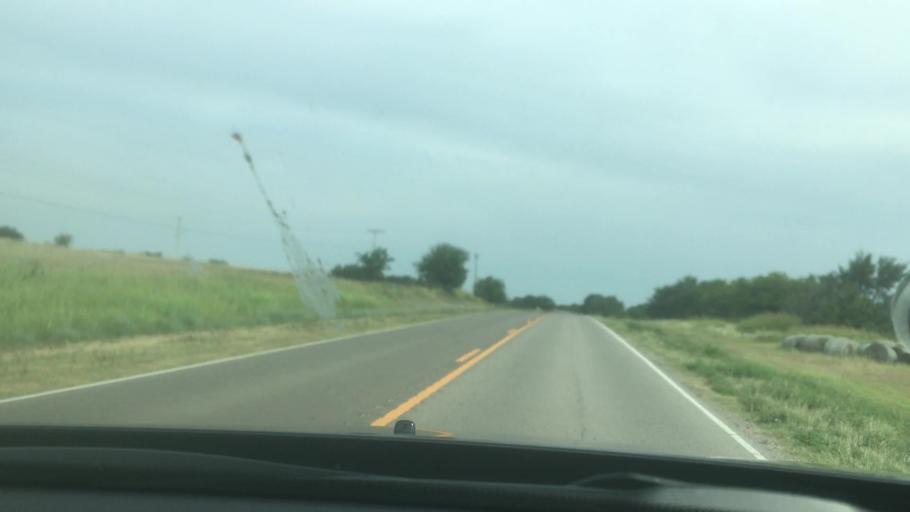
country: US
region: Oklahoma
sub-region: Garvin County
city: Maysville
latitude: 34.8075
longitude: -97.3729
